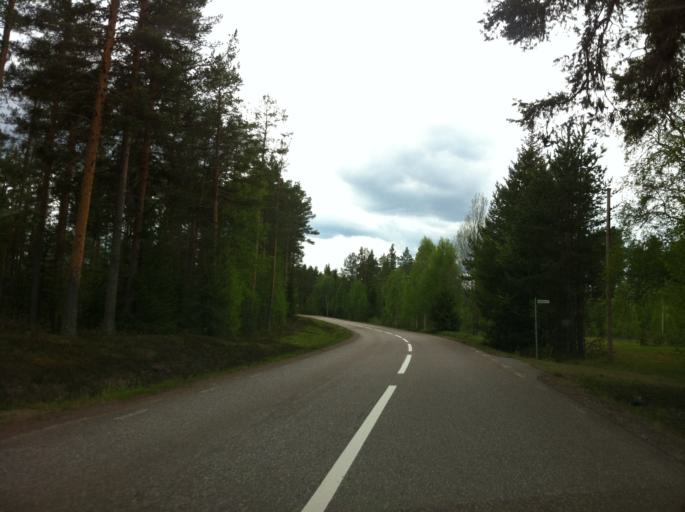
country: NO
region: Hedmark
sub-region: Trysil
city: Innbygda
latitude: 61.4360
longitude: 13.0990
